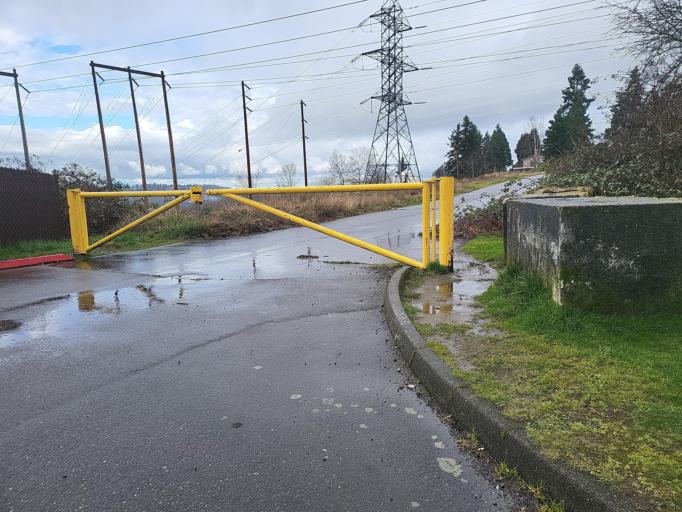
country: US
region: Washington
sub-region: King County
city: Renton
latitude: 47.4695
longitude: -122.1988
